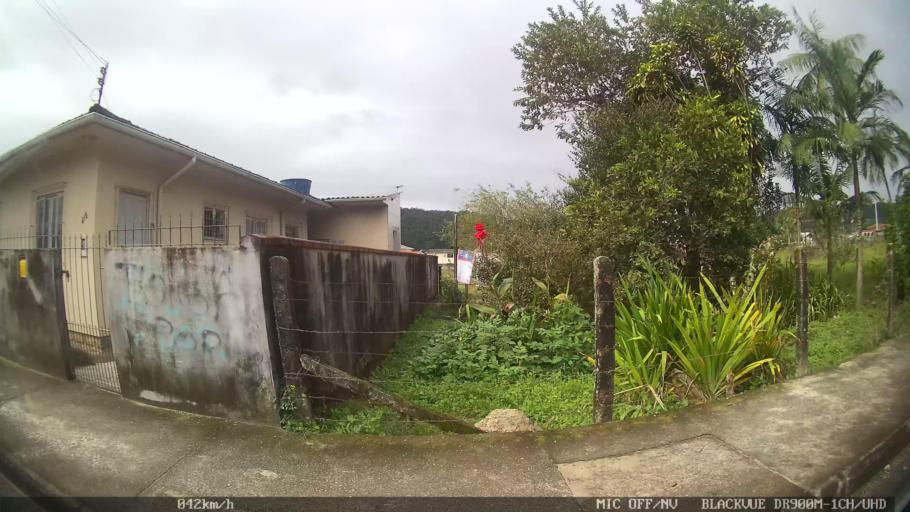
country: BR
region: Santa Catarina
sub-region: Biguacu
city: Biguacu
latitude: -27.5185
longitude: -48.6566
